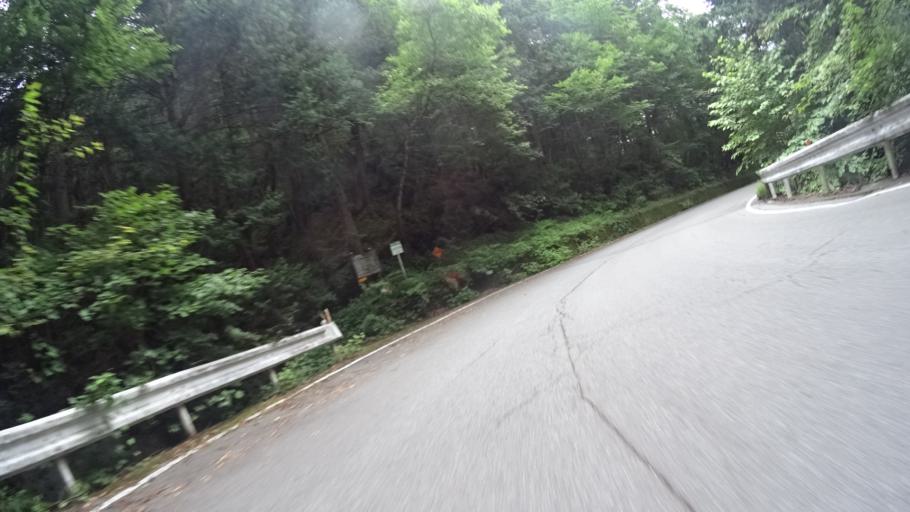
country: JP
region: Yamanashi
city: Enzan
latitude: 35.7955
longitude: 138.6844
